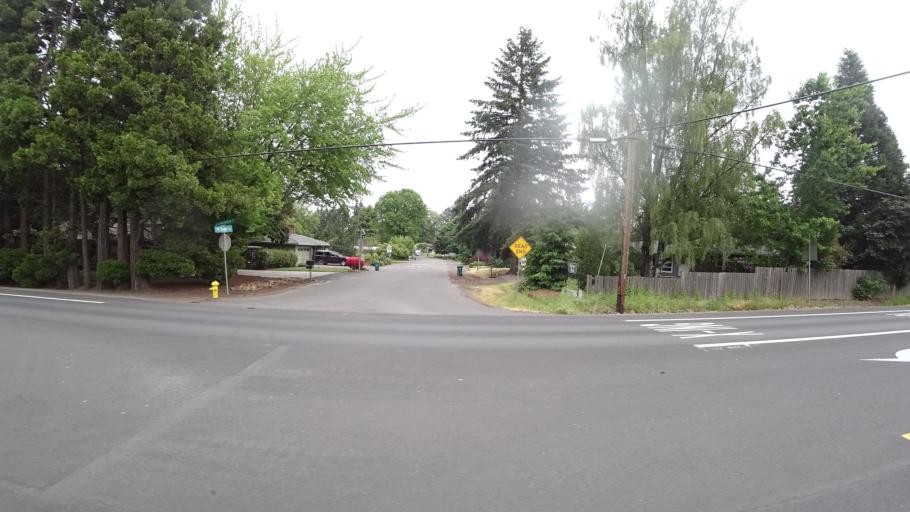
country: US
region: Oregon
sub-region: Washington County
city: Garden Home-Whitford
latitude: 45.4635
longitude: -122.7790
